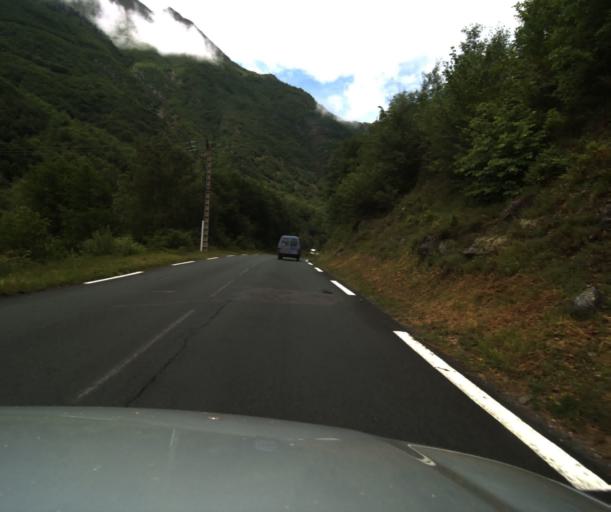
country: FR
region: Midi-Pyrenees
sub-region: Departement des Hautes-Pyrenees
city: Luz-Saint-Sauveur
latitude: 42.8090
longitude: 0.0094
